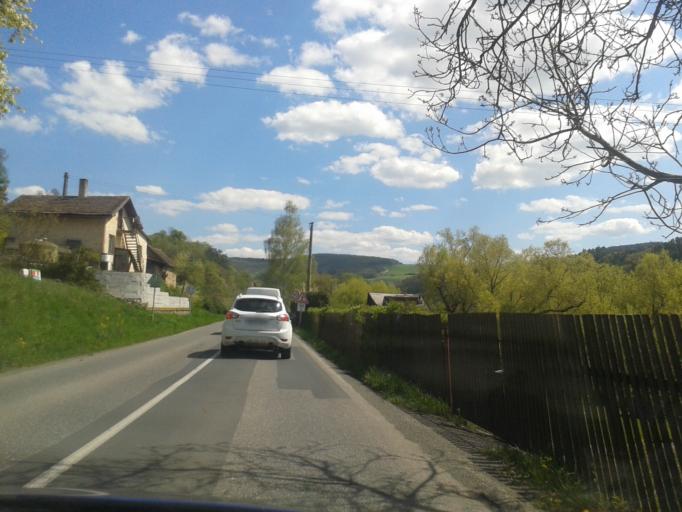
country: CZ
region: Central Bohemia
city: Nizbor
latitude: 49.9960
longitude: 14.0242
